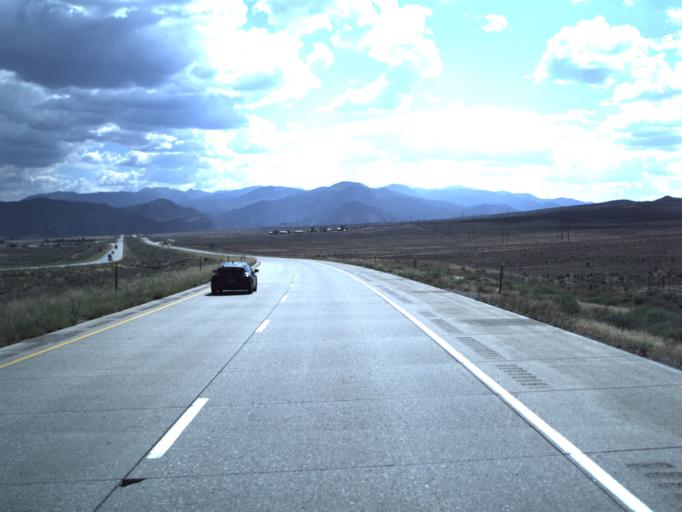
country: US
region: Utah
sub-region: Sevier County
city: Monroe
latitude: 38.6439
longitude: -112.2185
